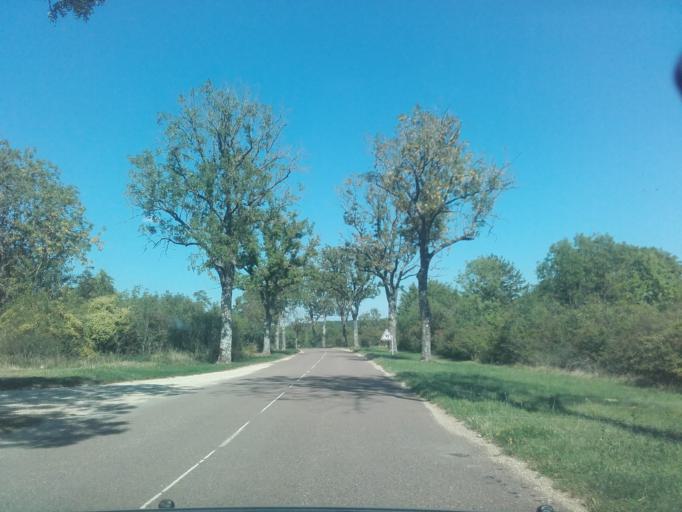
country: FR
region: Bourgogne
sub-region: Departement de la Cote-d'Or
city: Nolay
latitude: 46.9529
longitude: 4.6845
